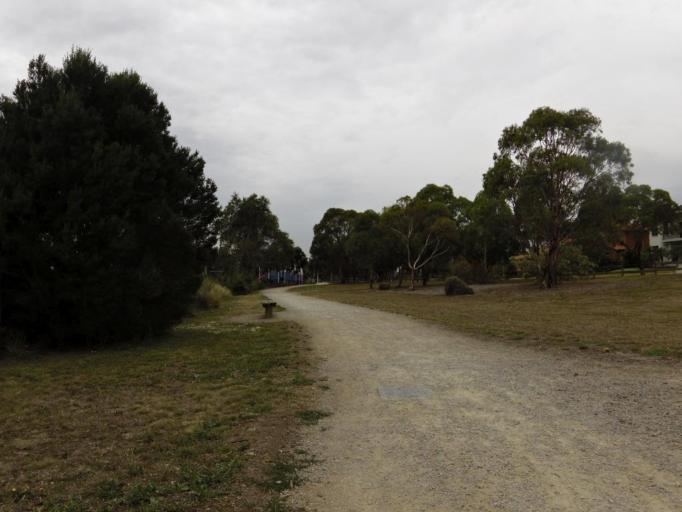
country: AU
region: Victoria
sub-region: Brimbank
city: Taylors Lakes
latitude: -37.7023
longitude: 144.7920
